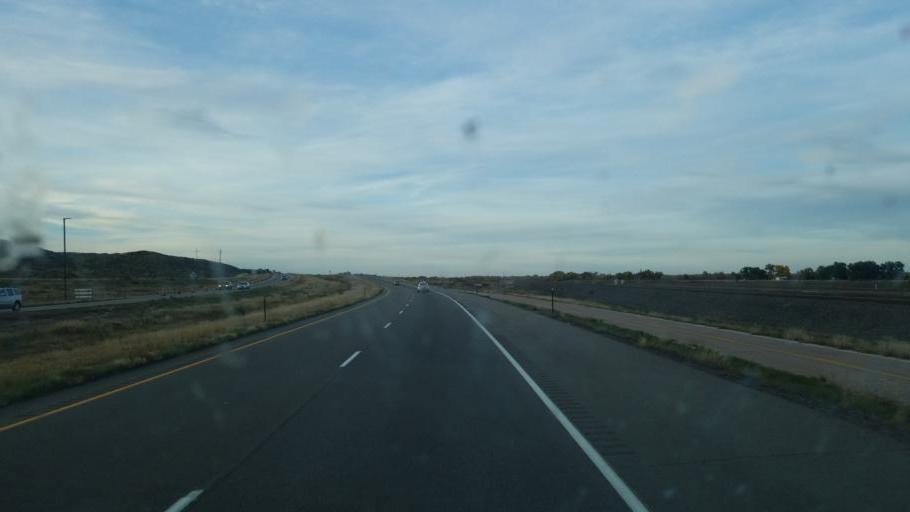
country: US
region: Colorado
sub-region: Pueblo County
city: Pueblo West
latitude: 38.4530
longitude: -104.6059
